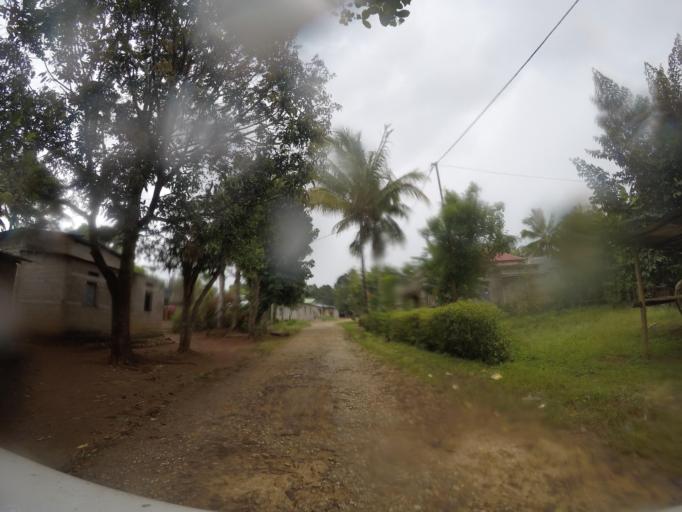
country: TL
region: Lautem
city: Lospalos
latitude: -8.5269
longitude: 126.9941
